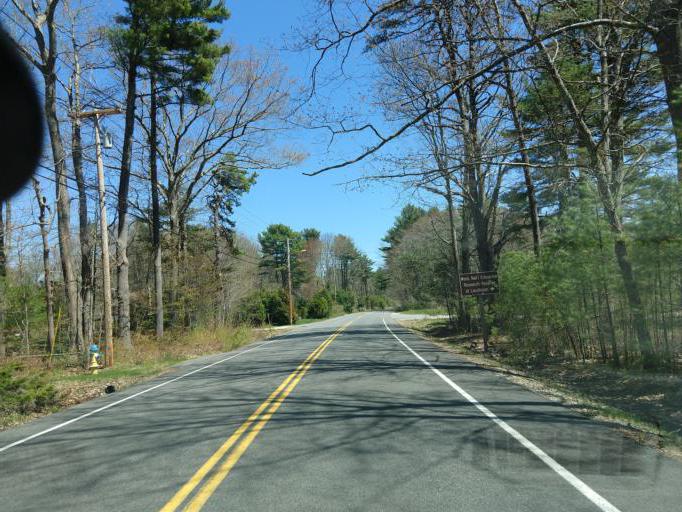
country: US
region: Maine
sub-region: York County
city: Kennebunk
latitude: 43.3471
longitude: -70.5521
